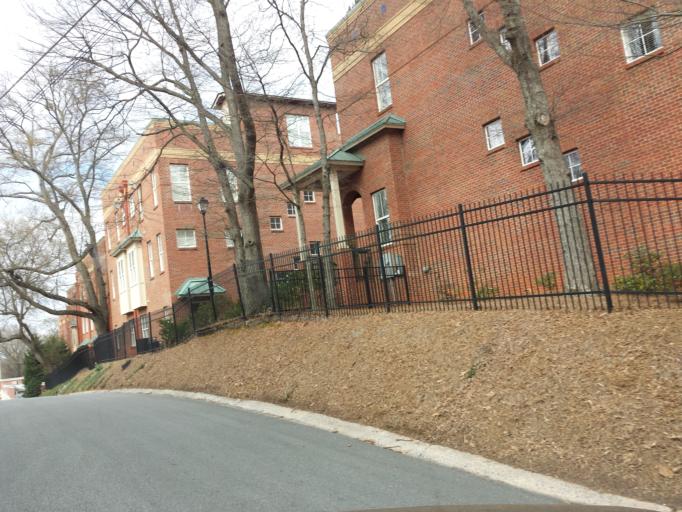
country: US
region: Georgia
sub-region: Cobb County
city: Marietta
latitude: 33.9480
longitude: -84.5424
